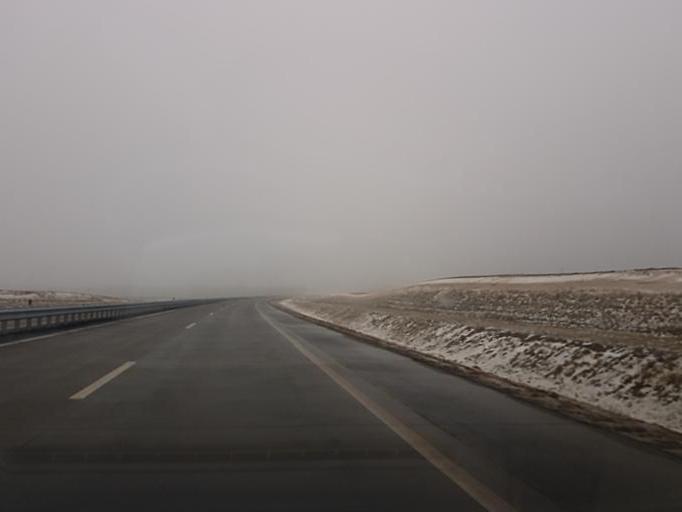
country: BY
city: Fanipol
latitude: 53.7632
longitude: 27.3817
